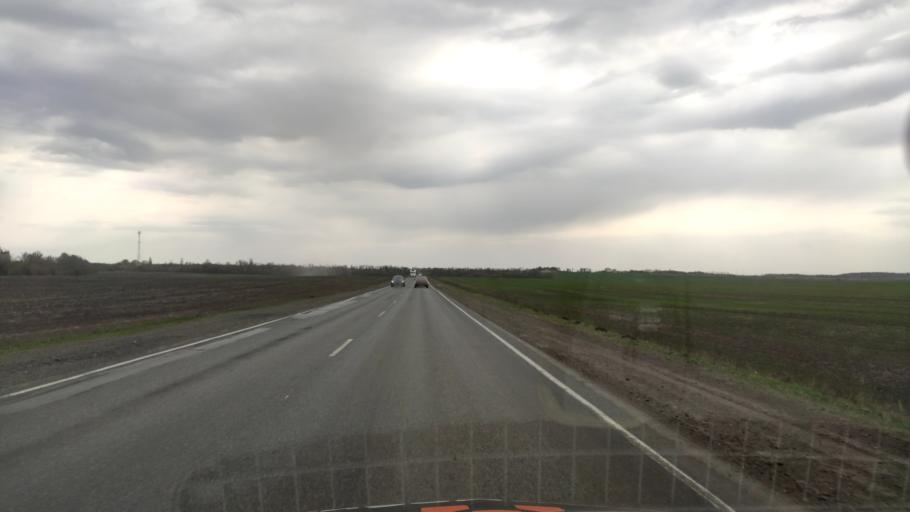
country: RU
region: Kursk
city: Gorshechnoye
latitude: 51.5487
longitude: 38.0290
